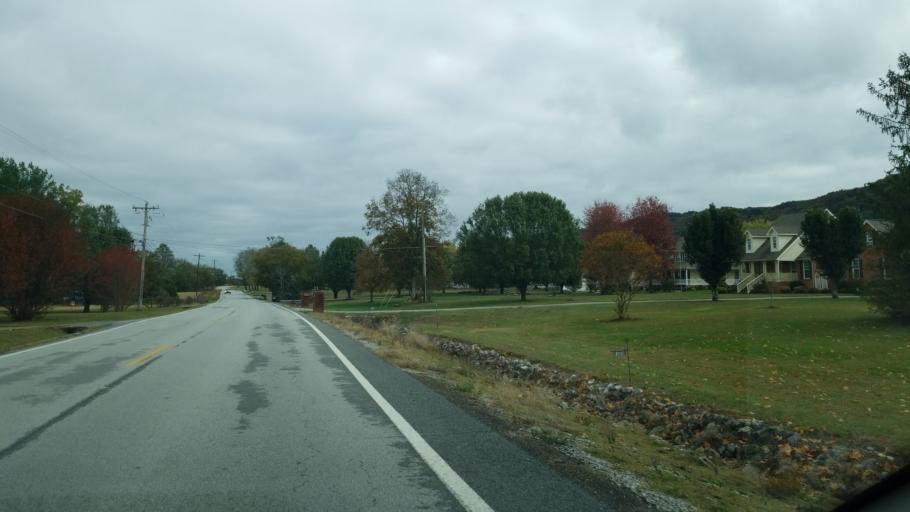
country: US
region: Tennessee
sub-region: Hamilton County
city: Lakesite
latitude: 35.1854
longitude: -85.0229
